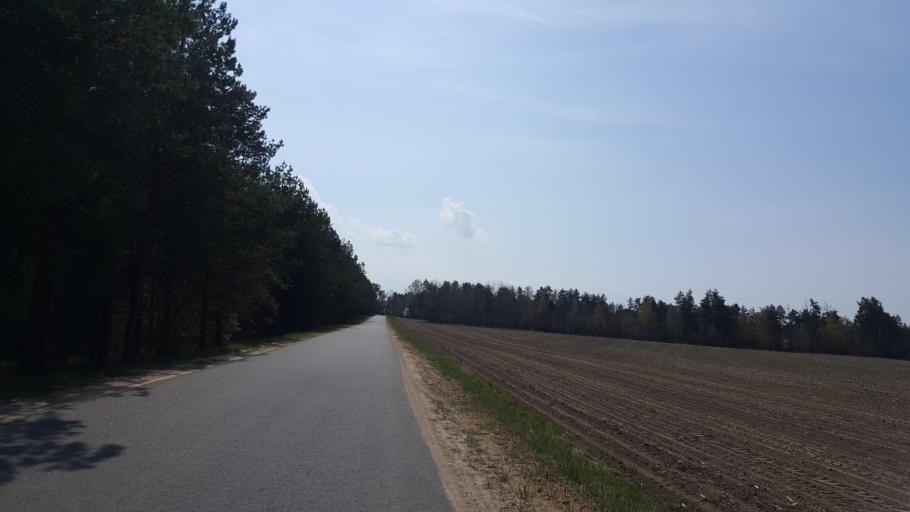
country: BY
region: Brest
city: Kamyanyets
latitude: 52.3344
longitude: 23.8261
